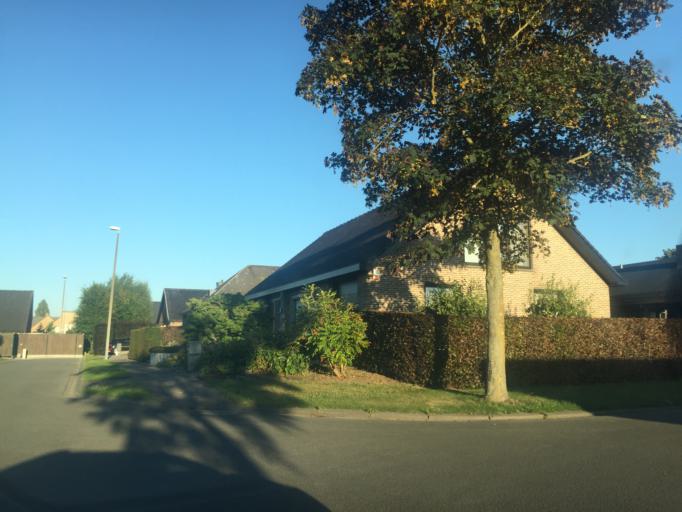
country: BE
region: Flanders
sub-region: Provincie West-Vlaanderen
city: Izegem
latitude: 50.9154
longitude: 3.2004
